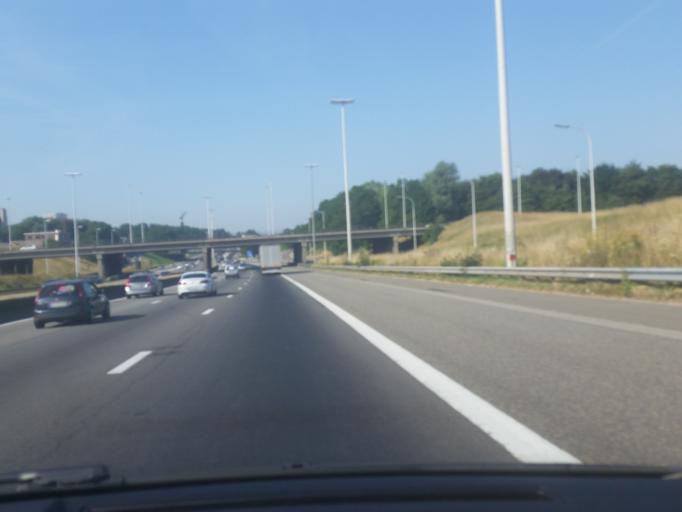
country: BE
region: Flanders
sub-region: Provincie Vlaams-Brabant
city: Bever
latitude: 50.9039
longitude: 4.3282
